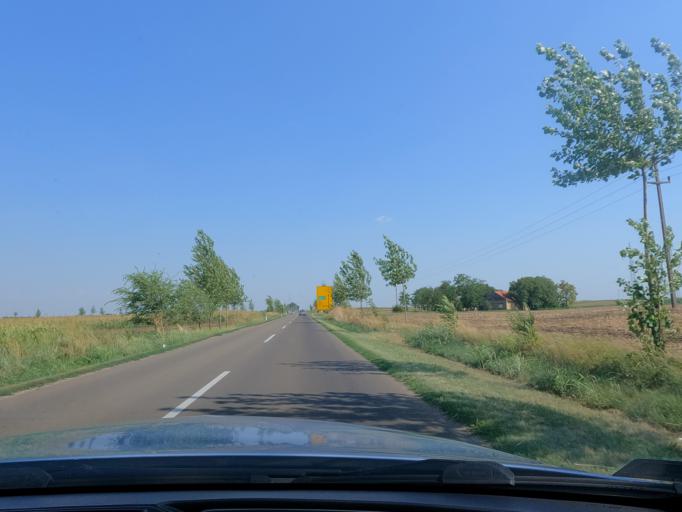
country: RS
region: Autonomna Pokrajina Vojvodina
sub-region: Severnobacki Okrug
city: Backa Topola
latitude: 45.8012
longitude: 19.6572
